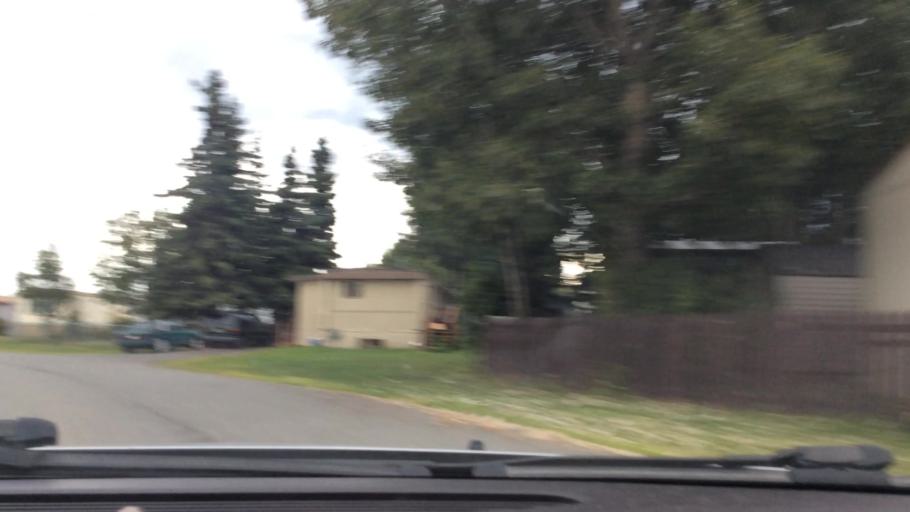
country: US
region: Alaska
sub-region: Anchorage Municipality
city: Anchorage
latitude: 61.1334
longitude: -149.8539
